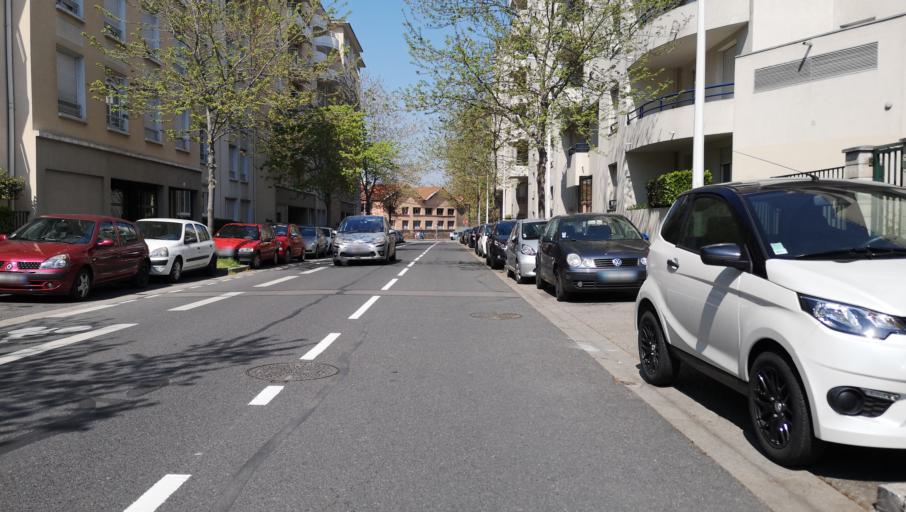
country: FR
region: Rhone-Alpes
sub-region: Departement du Rhone
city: Tassin-la-Demi-Lune
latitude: 45.7725
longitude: 4.8000
